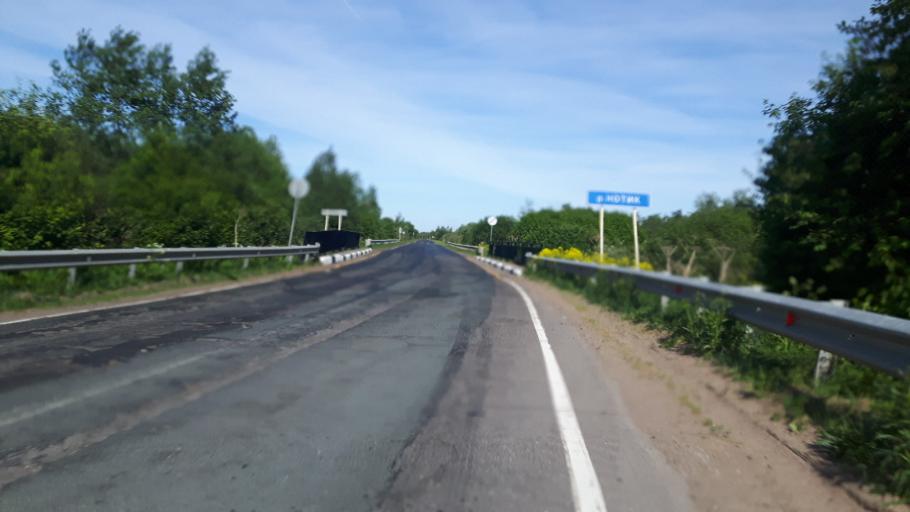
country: RU
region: Leningrad
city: Ivangorod
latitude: 59.4152
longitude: 28.3294
